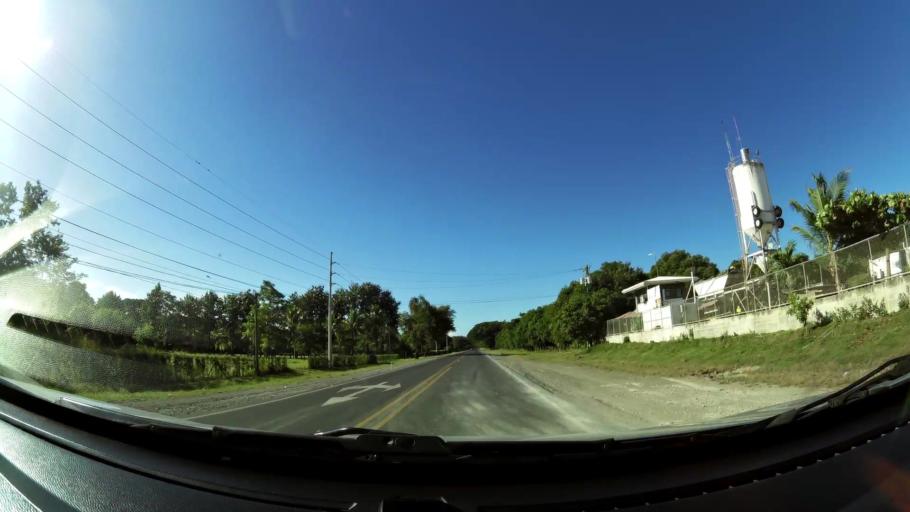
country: CR
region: Guanacaste
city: Belen
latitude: 10.4221
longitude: -85.5732
